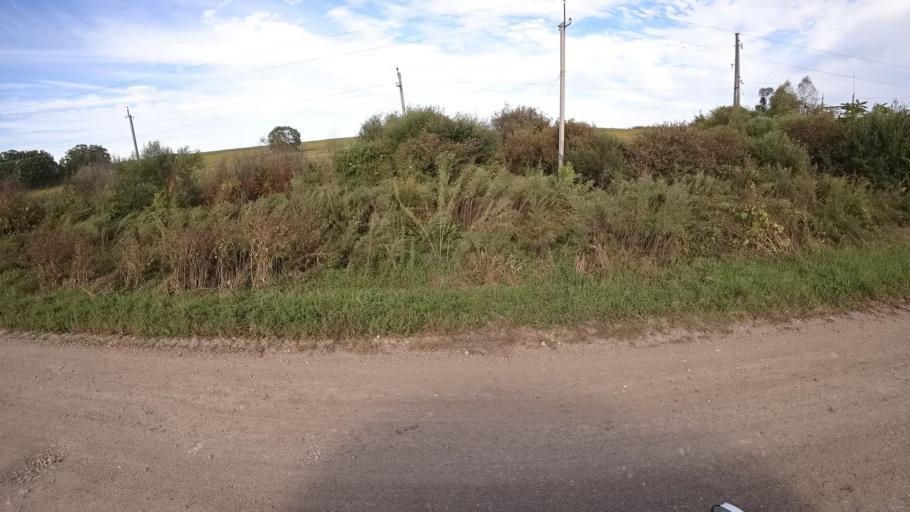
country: RU
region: Primorskiy
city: Dostoyevka
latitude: 44.3085
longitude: 133.4652
